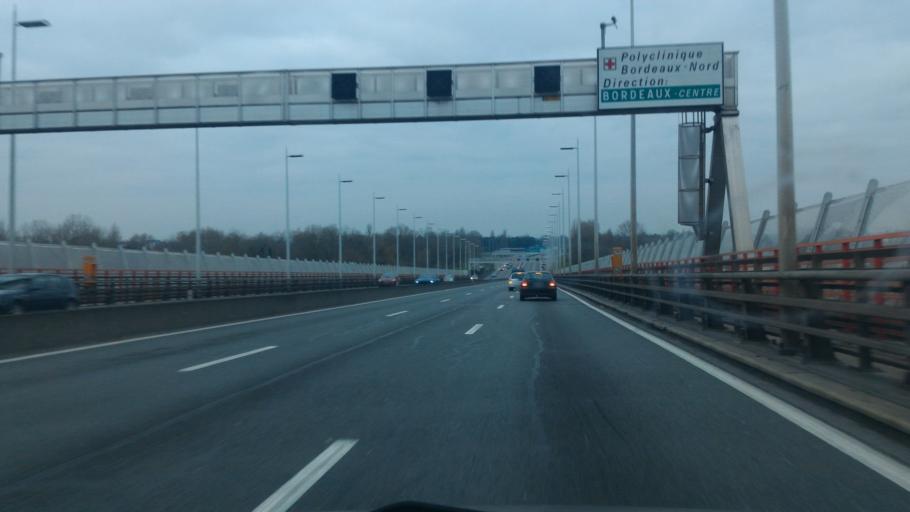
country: FR
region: Aquitaine
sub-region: Departement de la Gironde
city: Lormont
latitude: 44.8824
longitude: -0.5500
